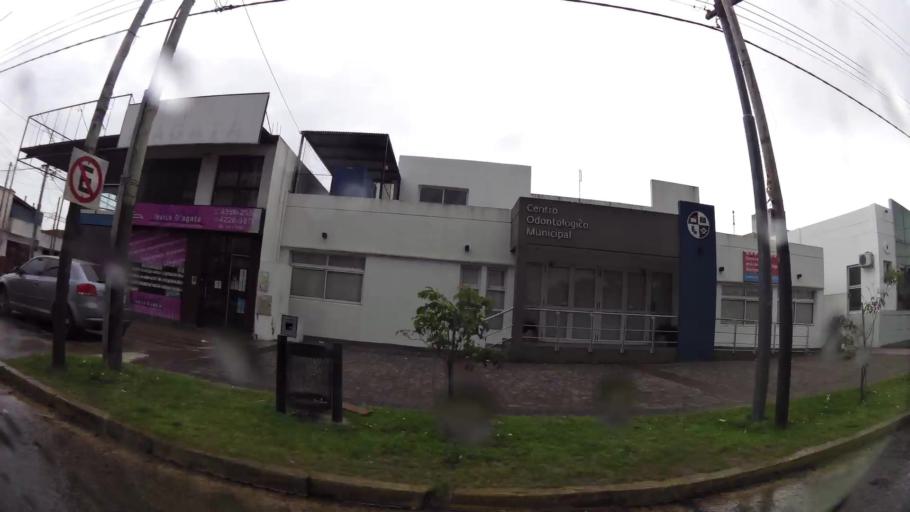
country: AR
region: Buenos Aires
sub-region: Partido de Quilmes
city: Quilmes
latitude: -34.7713
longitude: -58.2274
